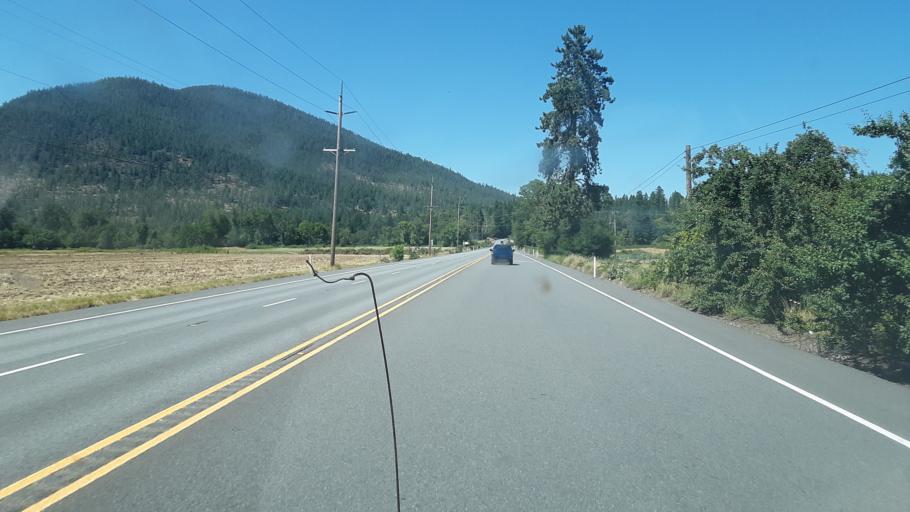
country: US
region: Oregon
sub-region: Josephine County
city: Cave Junction
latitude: 42.2211
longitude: -123.6476
